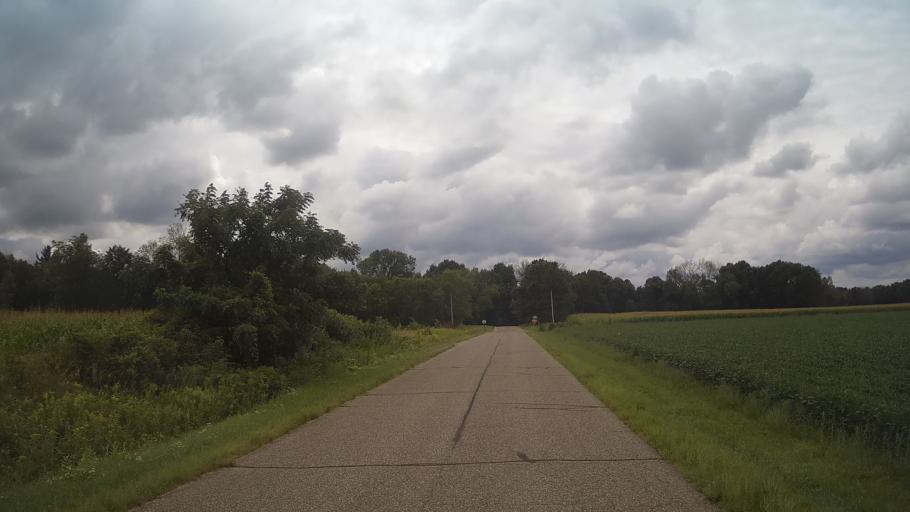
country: US
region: Wisconsin
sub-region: Adams County
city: Friendship
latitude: 44.0263
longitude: -89.9177
